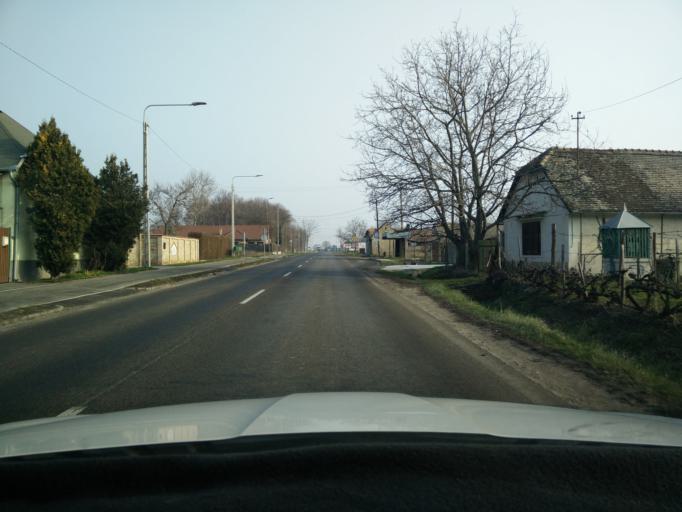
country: HU
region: Tolna
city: Szekszard
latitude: 46.3178
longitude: 18.6966
